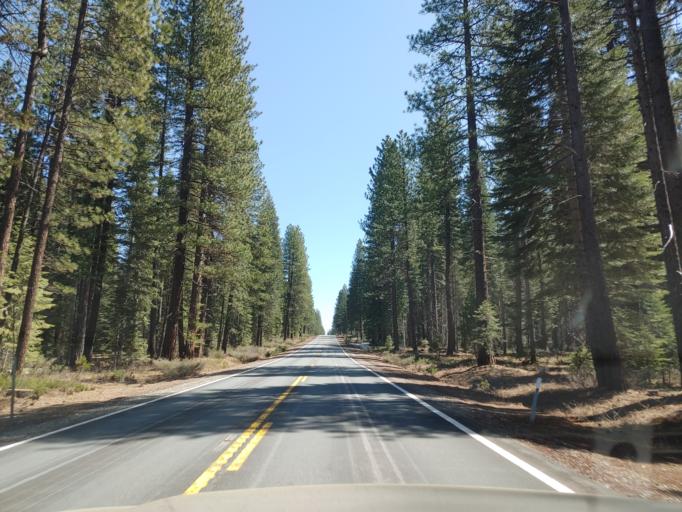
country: US
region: California
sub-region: Siskiyou County
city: McCloud
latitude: 41.2673
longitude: -121.9034
